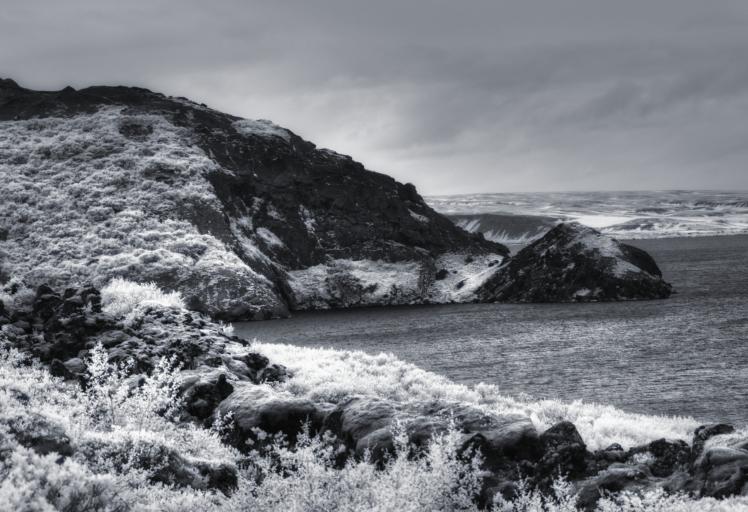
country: IS
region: South
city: Hveragerdi
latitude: 64.2310
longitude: -21.0513
